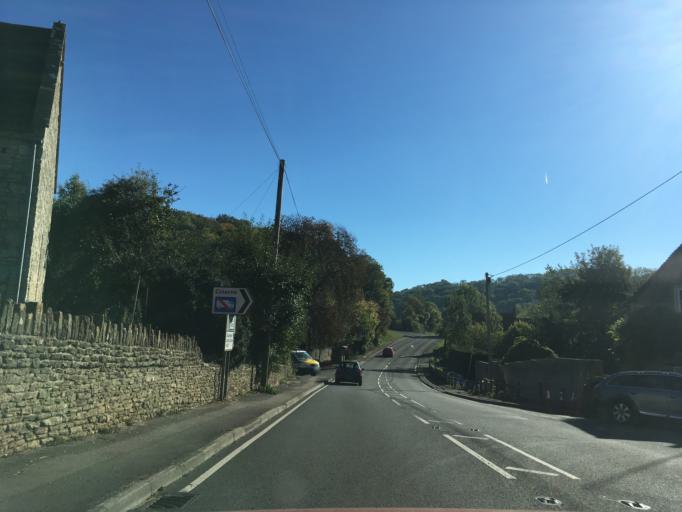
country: GB
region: England
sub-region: Wiltshire
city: Biddestone
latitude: 51.4727
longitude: -2.2295
